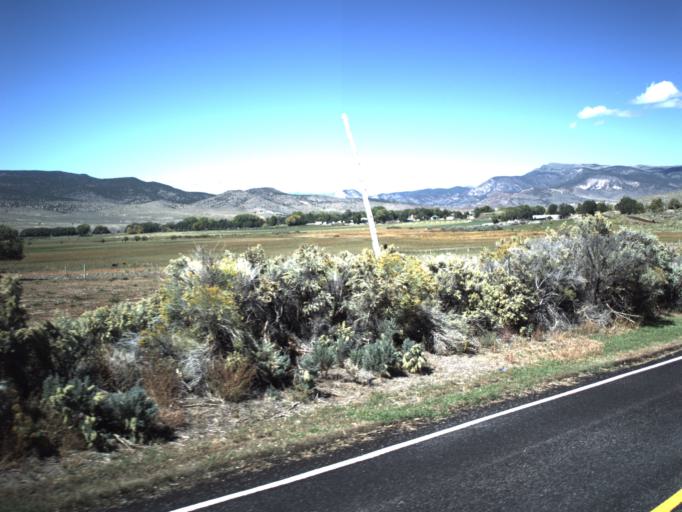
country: US
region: Utah
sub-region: Piute County
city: Junction
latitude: 38.1038
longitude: -111.9852
